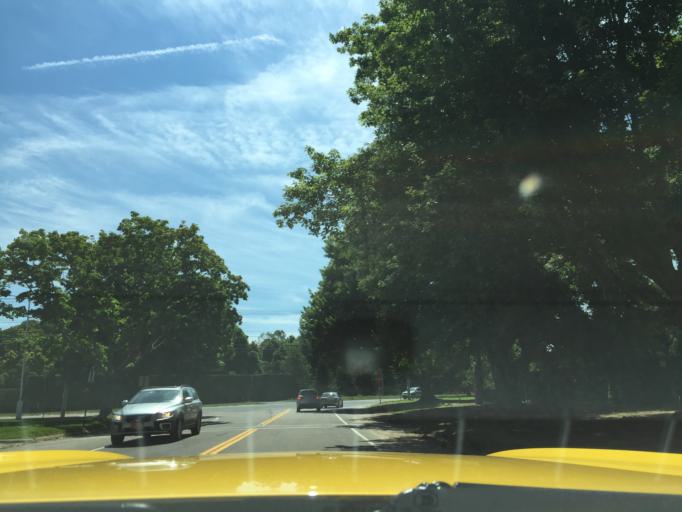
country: US
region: New York
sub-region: Suffolk County
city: Bridgehampton
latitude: 40.9292
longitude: -72.2794
